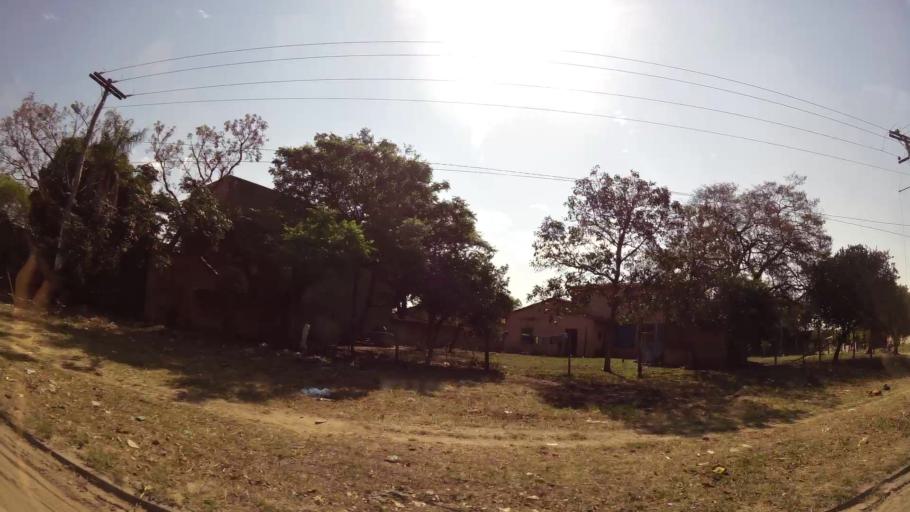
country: BO
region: Santa Cruz
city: Santa Cruz de la Sierra
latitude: -17.7639
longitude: -63.1121
